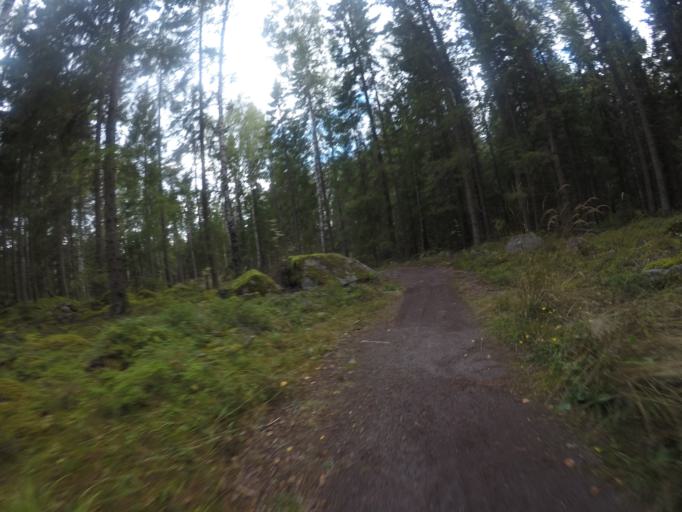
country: SE
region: Vaestmanland
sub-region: Vasteras
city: Hokasen
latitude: 59.6664
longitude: 16.5282
